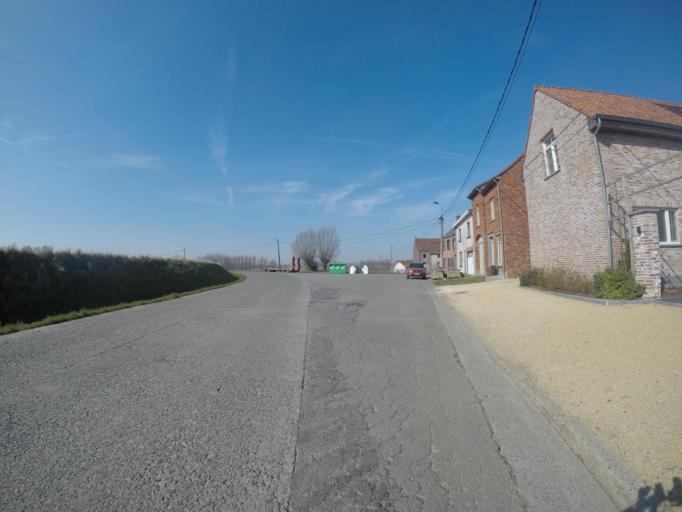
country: BE
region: Flanders
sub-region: Provincie Oost-Vlaanderen
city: Sint-Maria-Lierde
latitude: 50.7893
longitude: 3.8236
